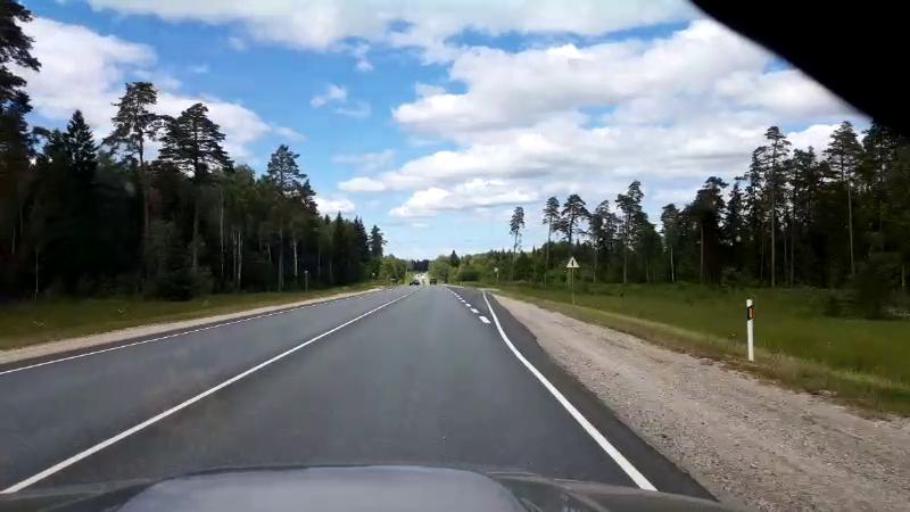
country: EE
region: Raplamaa
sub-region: Maerjamaa vald
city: Marjamaa
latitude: 59.0230
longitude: 24.4495
